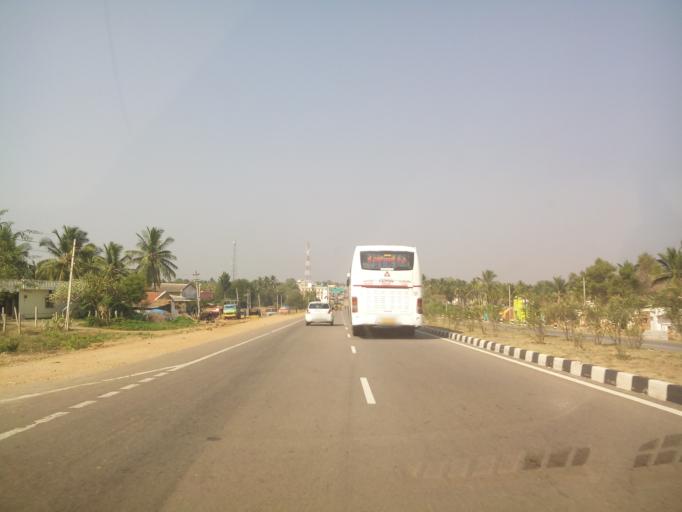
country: IN
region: Karnataka
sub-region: Mandya
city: Belluru
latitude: 12.9852
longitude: 76.8694
